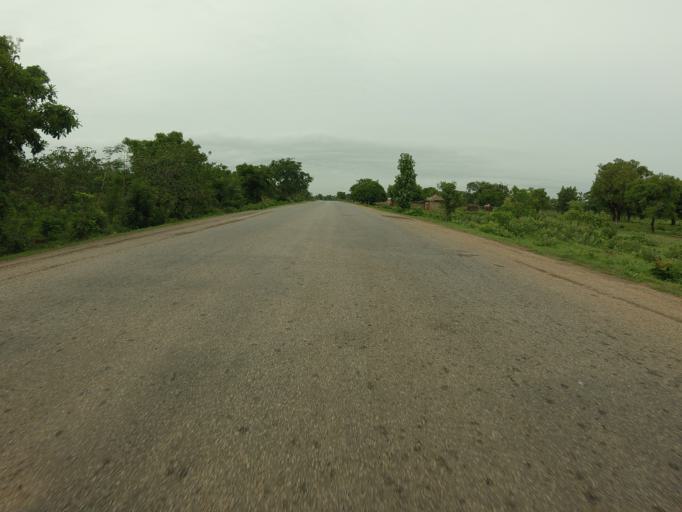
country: GH
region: Northern
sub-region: Yendi
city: Yendi
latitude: 9.5188
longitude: -0.0289
